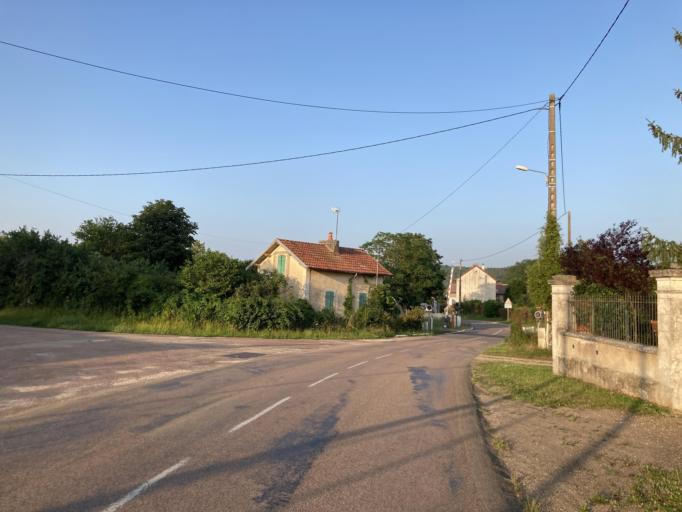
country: FR
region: Bourgogne
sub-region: Departement de l'Yonne
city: Vermenton
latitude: 47.6033
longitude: 3.6737
